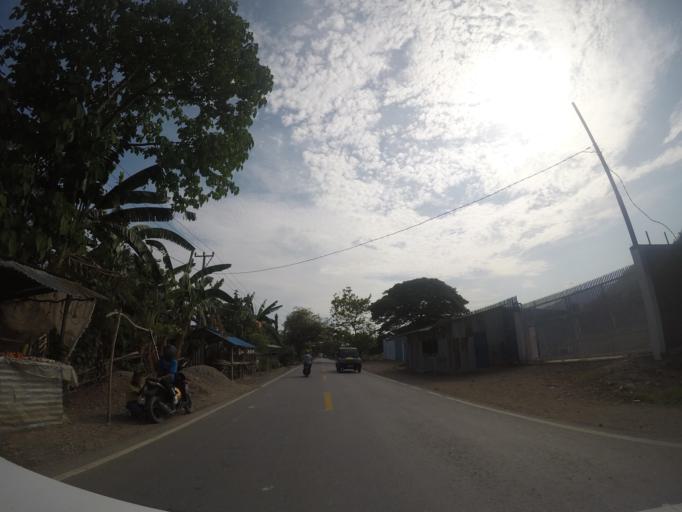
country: ID
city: Metinaro
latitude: -8.5487
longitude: 125.6655
